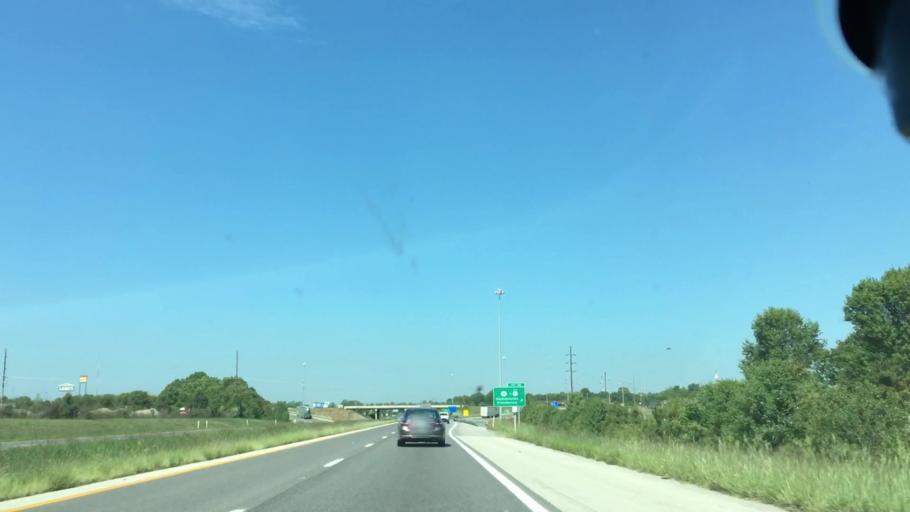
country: US
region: Kentucky
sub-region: Hopkins County
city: Madisonville
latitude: 37.3491
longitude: -87.4835
